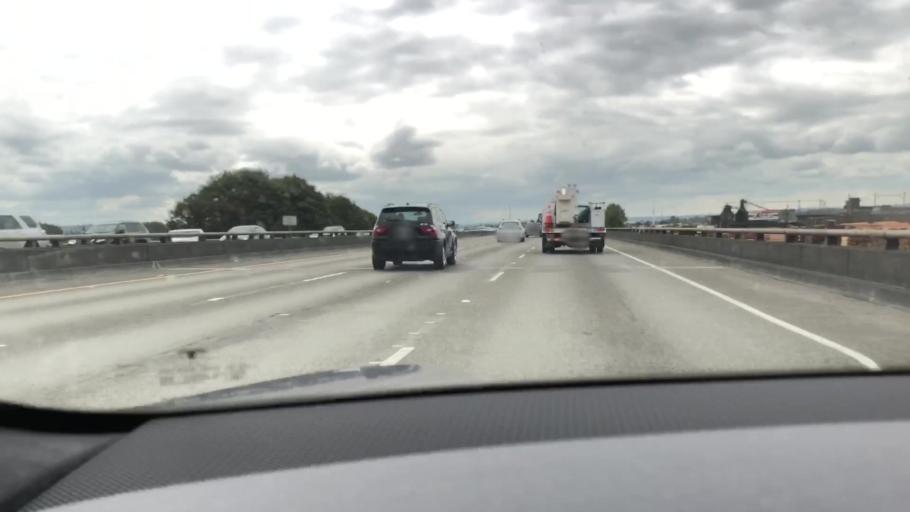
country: US
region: Washington
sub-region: Snohomish County
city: Marysville
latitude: 48.0239
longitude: -122.1760
